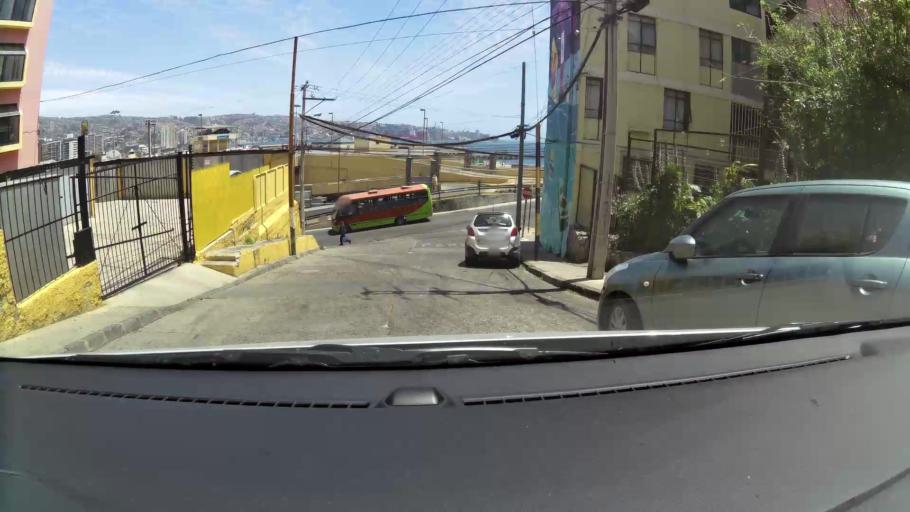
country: CL
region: Valparaiso
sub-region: Provincia de Valparaiso
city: Valparaiso
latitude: -33.0440
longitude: -71.6035
